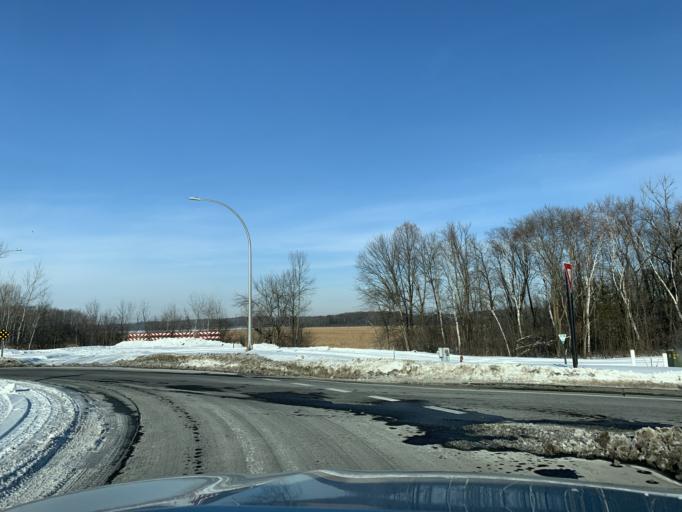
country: US
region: Minnesota
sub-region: Anoka County
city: Columbus
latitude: 45.2504
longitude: -93.0295
